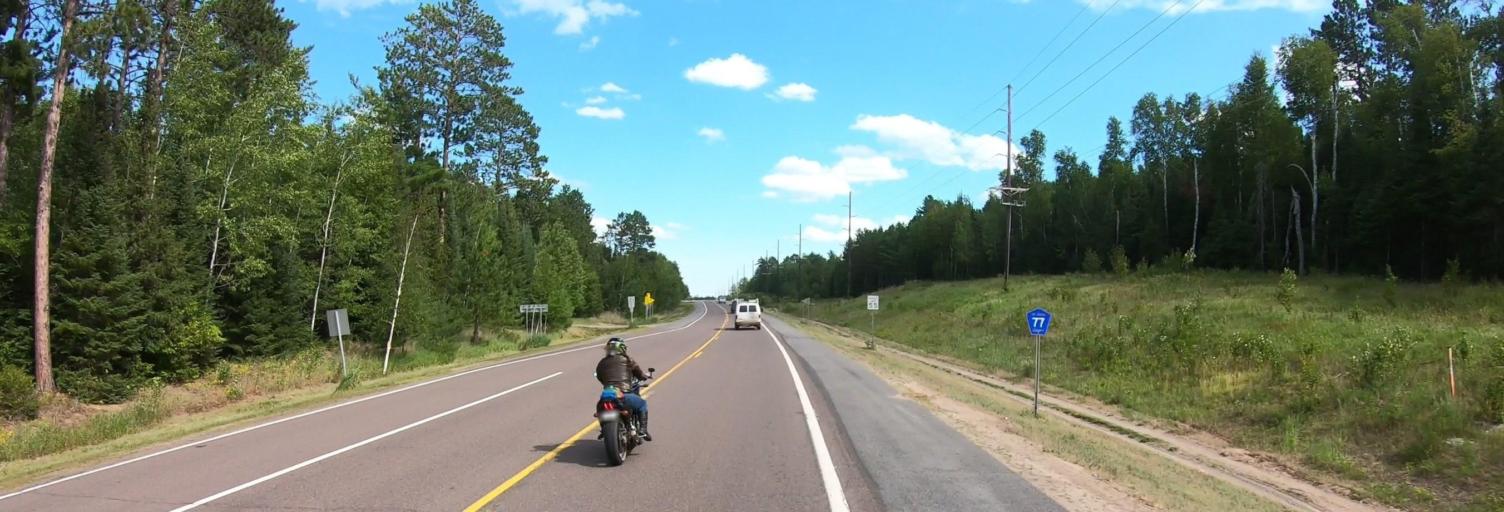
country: US
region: Minnesota
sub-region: Saint Louis County
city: Virginia
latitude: 47.8496
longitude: -92.3986
